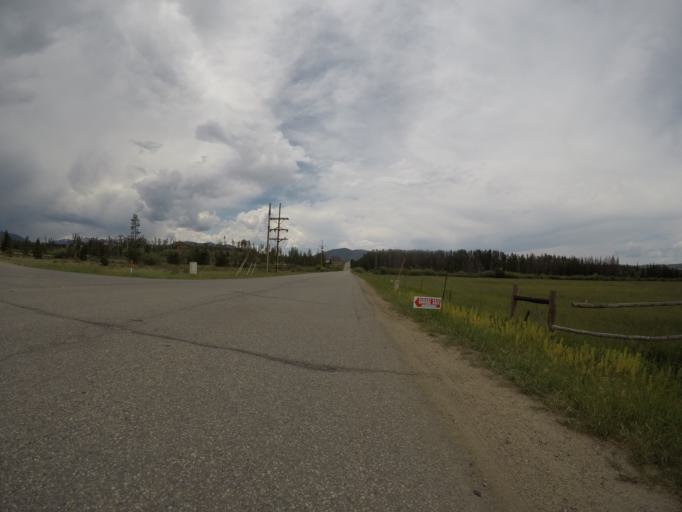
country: US
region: Colorado
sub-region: Grand County
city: Fraser
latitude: 39.9555
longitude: -105.8238
